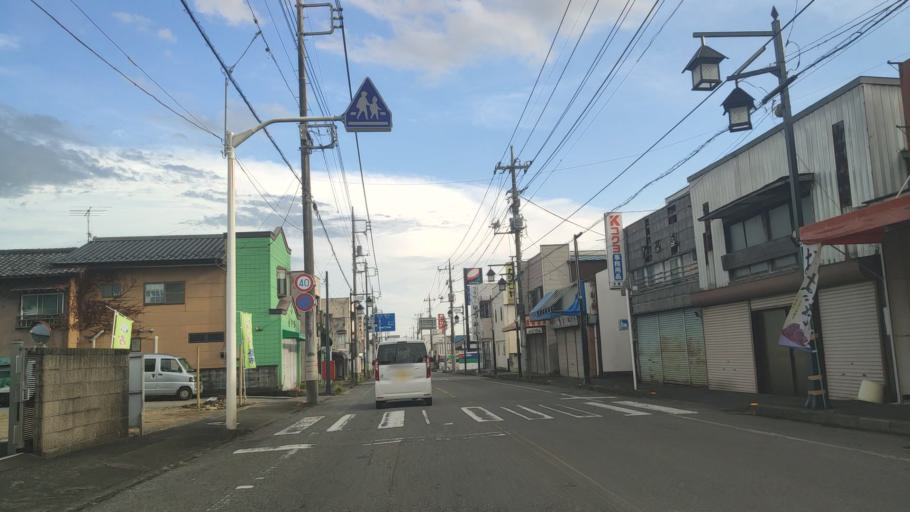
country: JP
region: Gunma
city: Omamacho-omama
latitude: 36.4318
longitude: 139.2750
